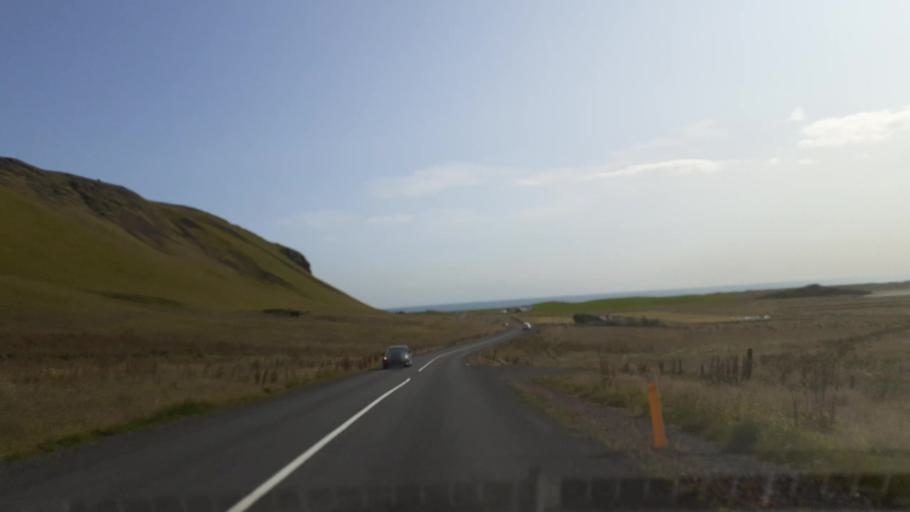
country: IS
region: South
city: Vestmannaeyjar
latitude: 63.4151
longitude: -19.0482
